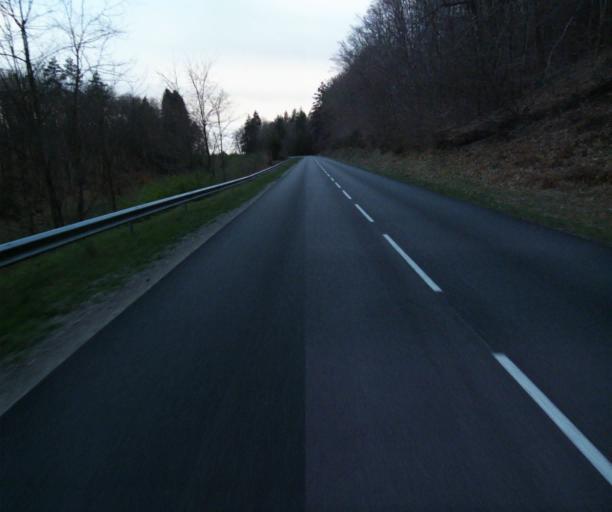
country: FR
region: Limousin
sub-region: Departement de la Correze
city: Correze
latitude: 45.3520
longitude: 1.8768
